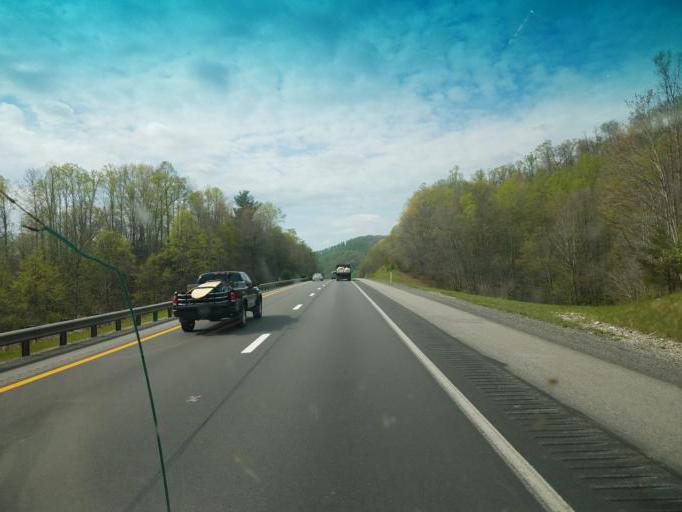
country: US
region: West Virginia
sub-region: Raleigh County
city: Bradley
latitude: 37.8899
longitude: -81.2671
